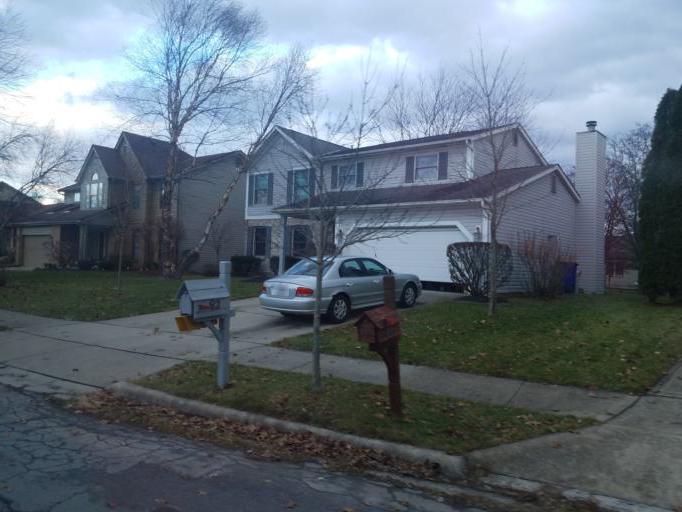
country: US
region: Ohio
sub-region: Delaware County
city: Delaware
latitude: 40.3116
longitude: -83.1007
